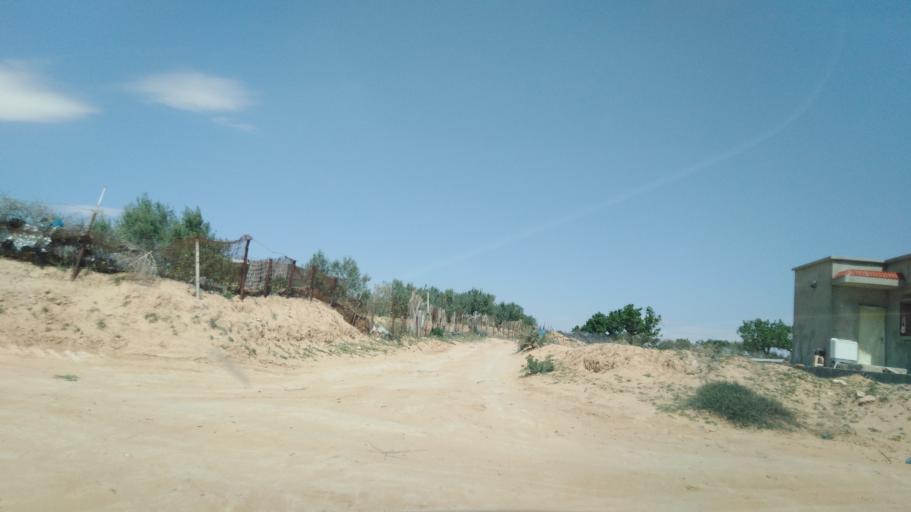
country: TN
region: Safaqis
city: Sfax
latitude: 34.7645
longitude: 10.5193
